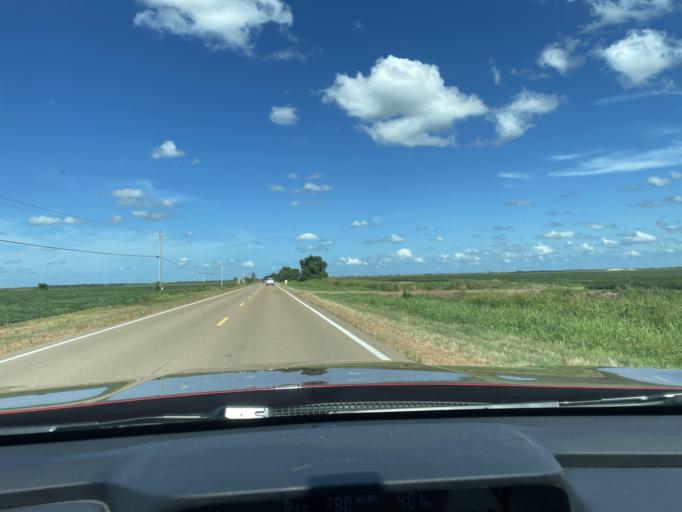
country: US
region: Mississippi
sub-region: Humphreys County
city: Belzoni
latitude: 33.1837
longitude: -90.5446
